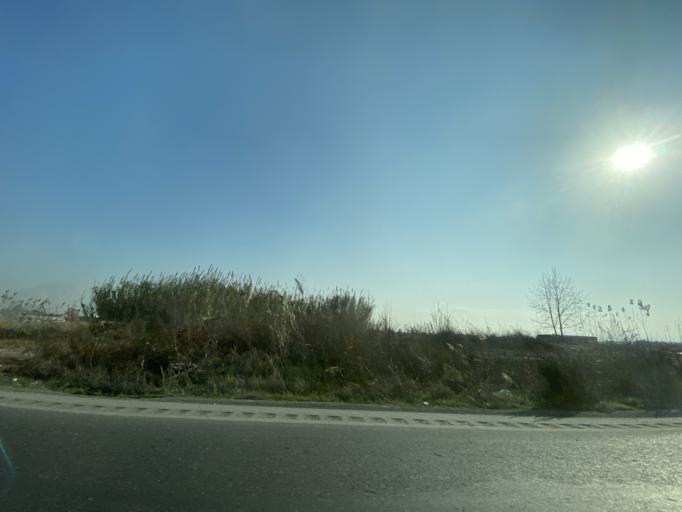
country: IR
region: Mazandaran
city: Amol
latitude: 36.4906
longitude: 52.4966
